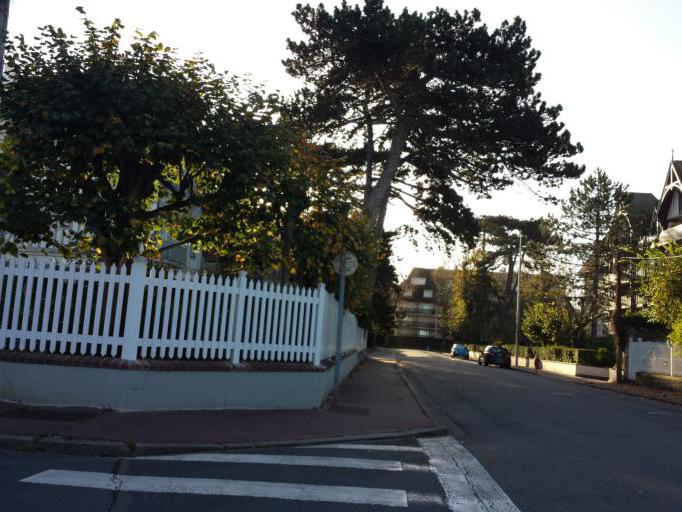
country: FR
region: Lower Normandy
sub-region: Departement du Calvados
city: Deauville
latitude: 49.3543
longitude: 0.0625
